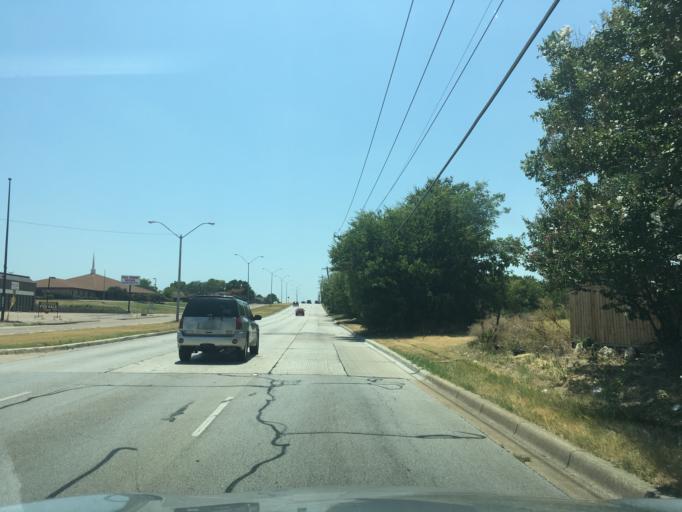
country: US
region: Texas
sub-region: Tarrant County
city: Edgecliff Village
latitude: 32.6425
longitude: -97.3698
